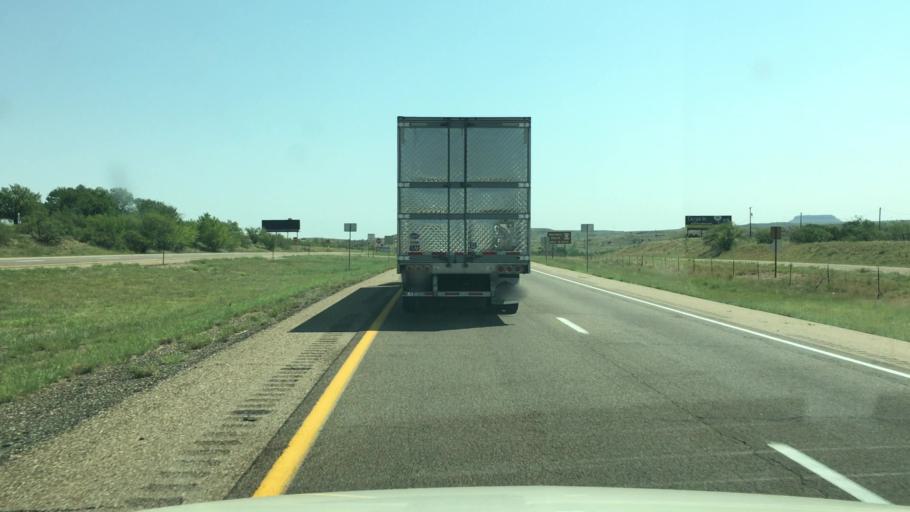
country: US
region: New Mexico
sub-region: Quay County
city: Tucumcari
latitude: 35.1467
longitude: -103.8002
